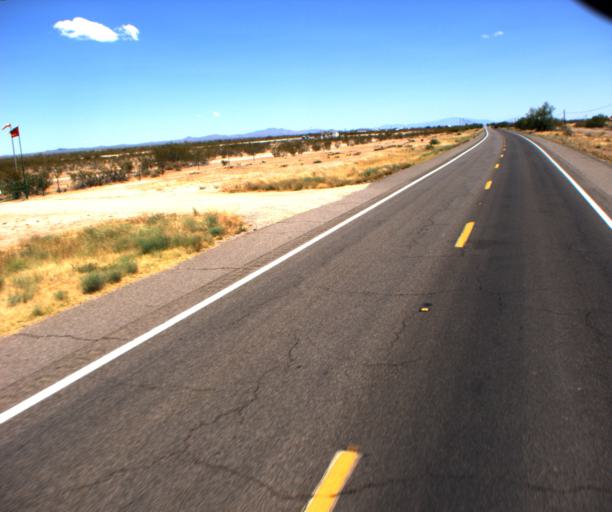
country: US
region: Arizona
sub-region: Pinal County
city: Florence
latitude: 32.9874
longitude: -111.3611
